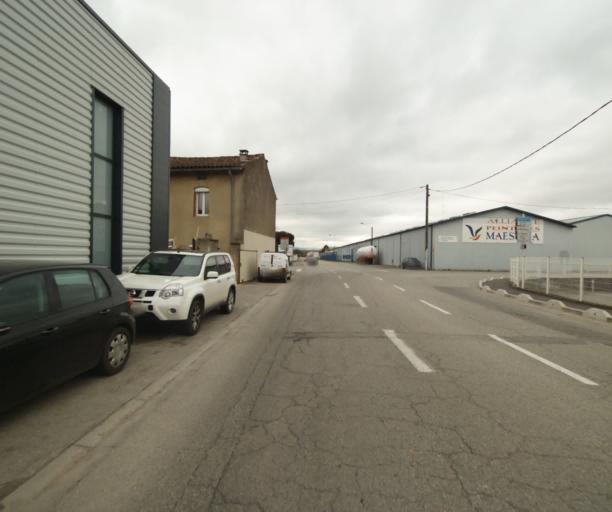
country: FR
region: Midi-Pyrenees
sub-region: Departement de l'Ariege
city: Pamiers
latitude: 43.1218
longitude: 1.6212
